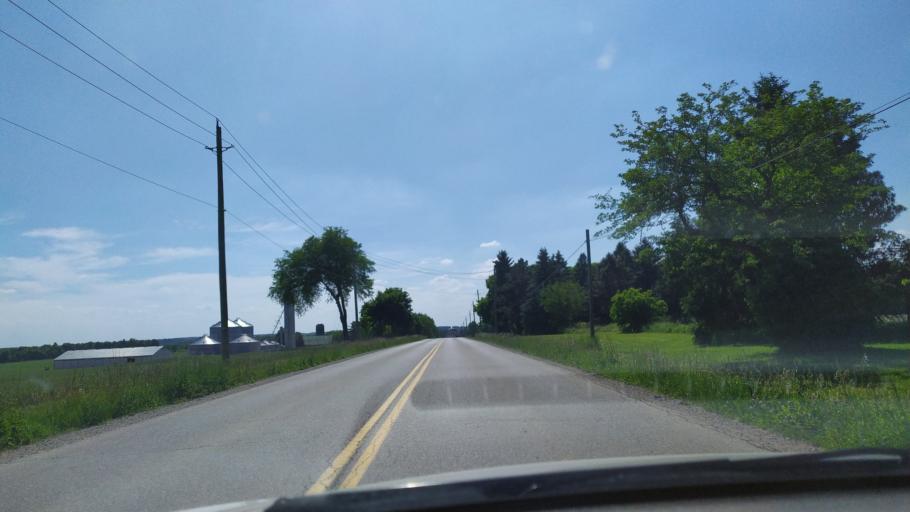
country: CA
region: Ontario
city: Kitchener
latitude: 43.3770
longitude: -80.5202
